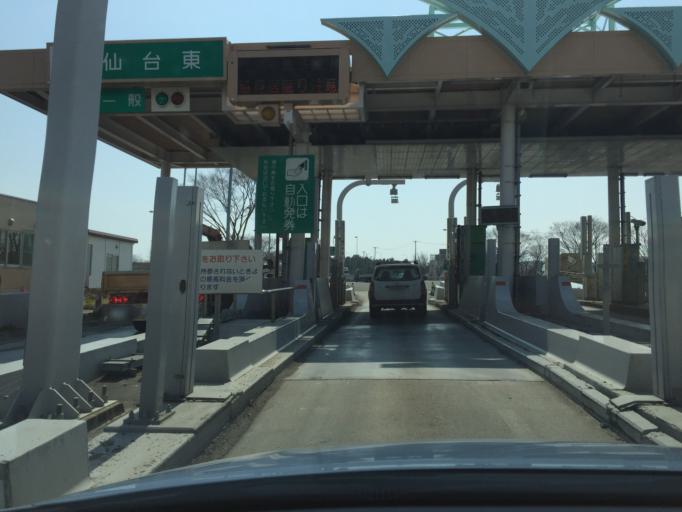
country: JP
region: Miyagi
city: Sendai-shi
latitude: 38.2476
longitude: 140.9520
